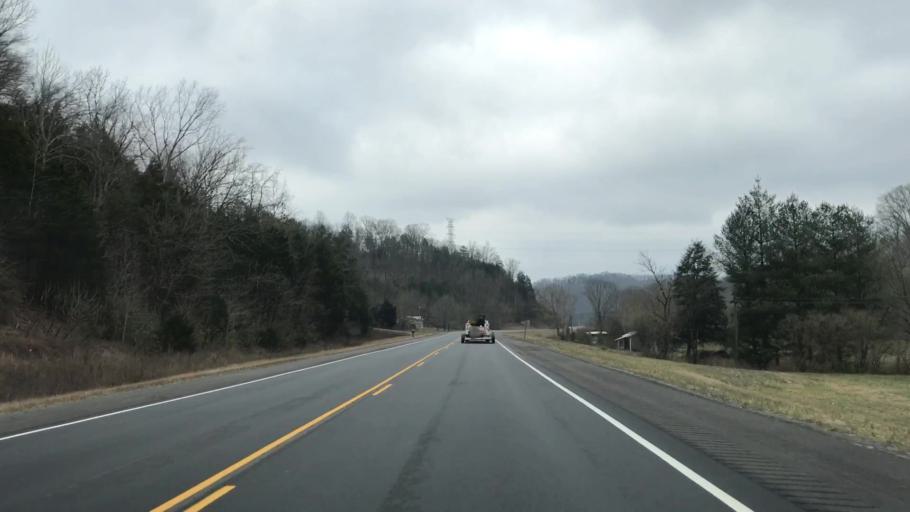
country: US
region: Kentucky
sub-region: Cumberland County
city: Burkesville
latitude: 36.8939
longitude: -85.4265
